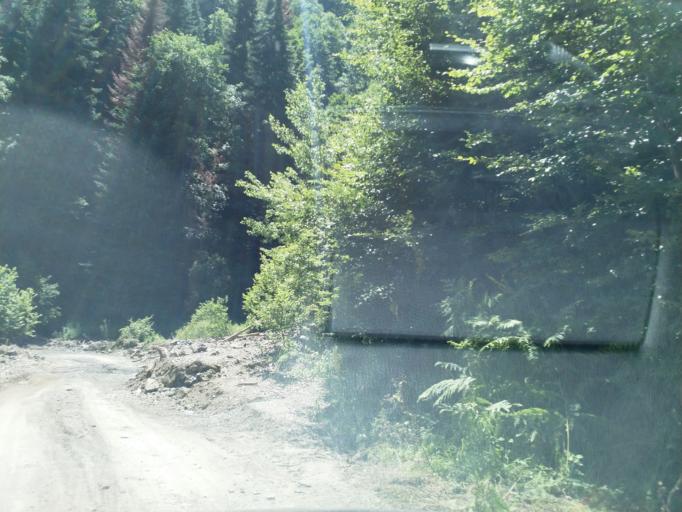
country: XK
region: Mitrovica
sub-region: Komuna e Leposaviqit
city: Leposaviq
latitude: 43.2788
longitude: 20.8668
